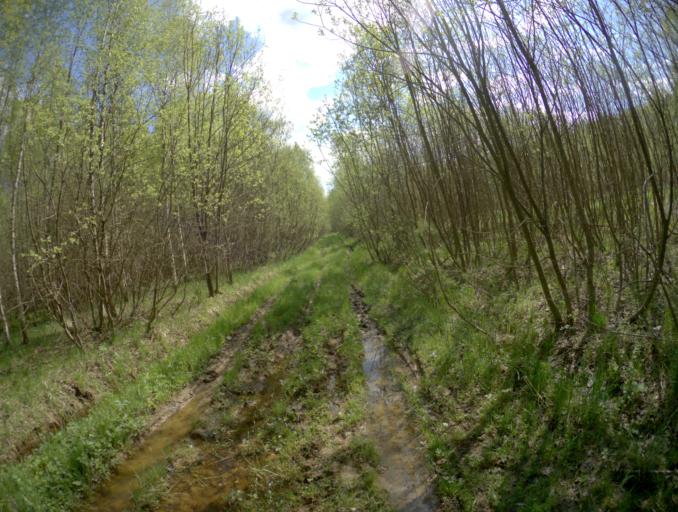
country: RU
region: Vladimir
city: Golovino
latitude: 55.9619
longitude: 40.3982
